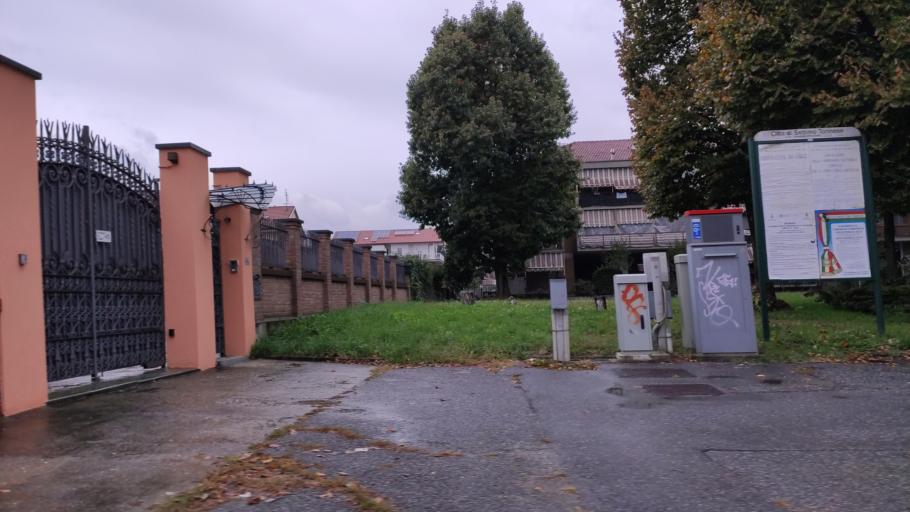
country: IT
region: Piedmont
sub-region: Provincia di Torino
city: Settimo Torinese
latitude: 45.1439
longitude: 7.7679
